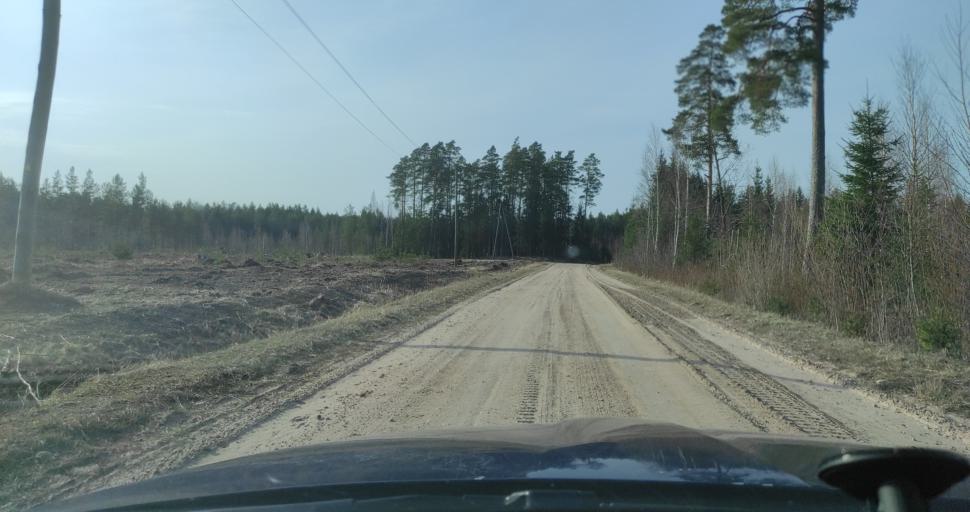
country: LV
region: Kuldigas Rajons
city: Kuldiga
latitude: 57.0138
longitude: 22.0137
